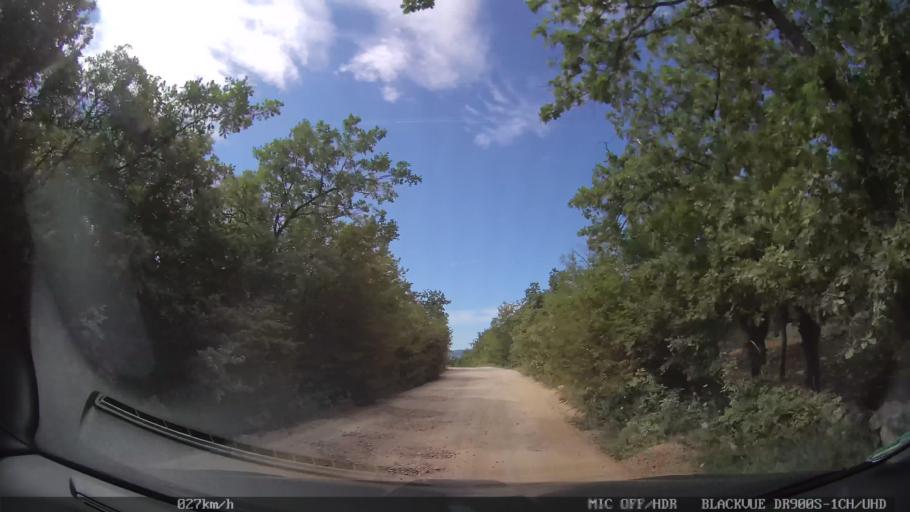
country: HR
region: Primorsko-Goranska
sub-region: Grad Krk
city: Krk
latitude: 45.0351
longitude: 14.5287
